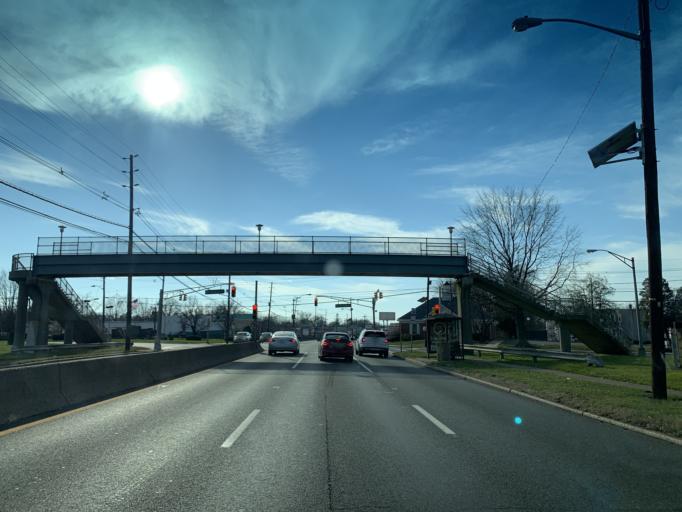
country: US
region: New Jersey
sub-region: Camden County
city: Pennsauken
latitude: 39.9566
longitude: -75.0576
